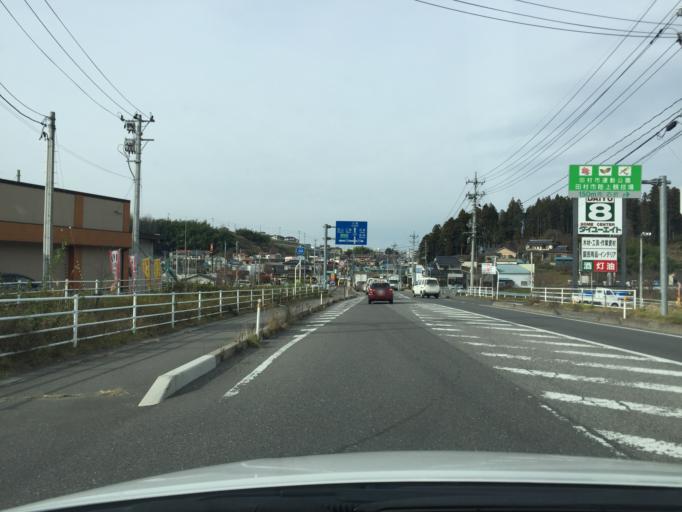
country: JP
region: Fukushima
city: Funehikimachi-funehiki
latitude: 37.4352
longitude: 140.5929
